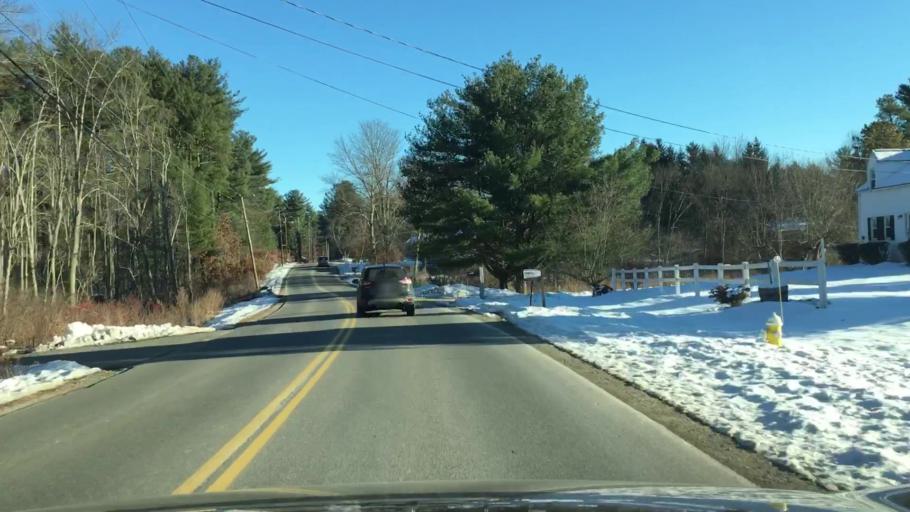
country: US
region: New Hampshire
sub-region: Hillsborough County
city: Hollis
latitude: 42.8131
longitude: -71.5664
